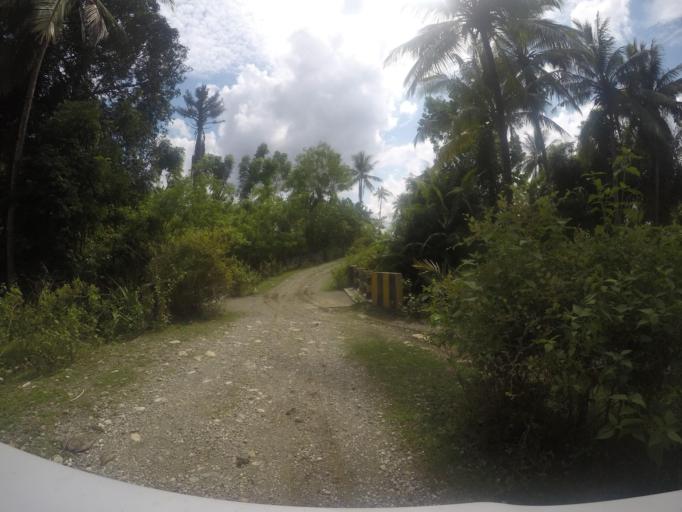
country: TL
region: Viqueque
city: Viqueque
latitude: -8.8495
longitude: 126.3627
